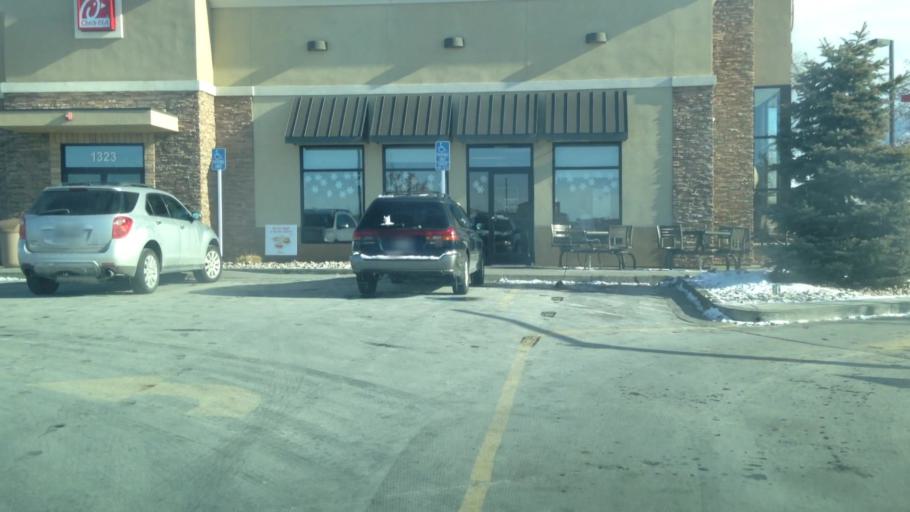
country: US
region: Utah
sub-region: Cache County
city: Logan
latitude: 41.7562
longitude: -111.8352
